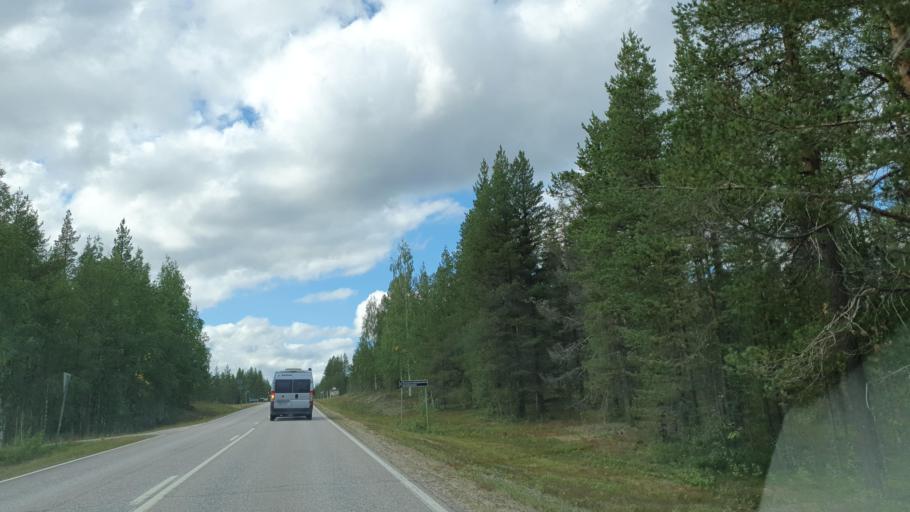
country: FI
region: Lapland
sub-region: Tunturi-Lappi
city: Muonio
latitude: 67.8612
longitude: 24.1113
